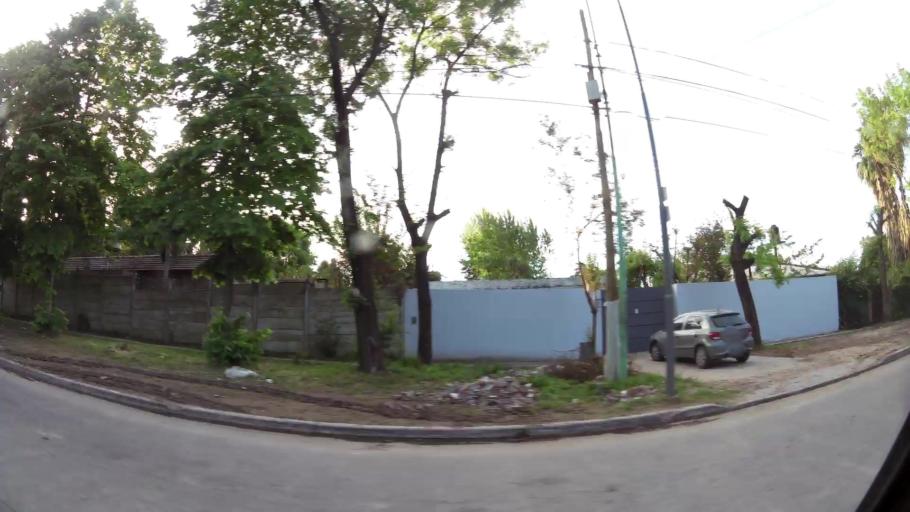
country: AR
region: Buenos Aires
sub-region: Partido de Quilmes
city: Quilmes
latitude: -34.7957
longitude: -58.1944
